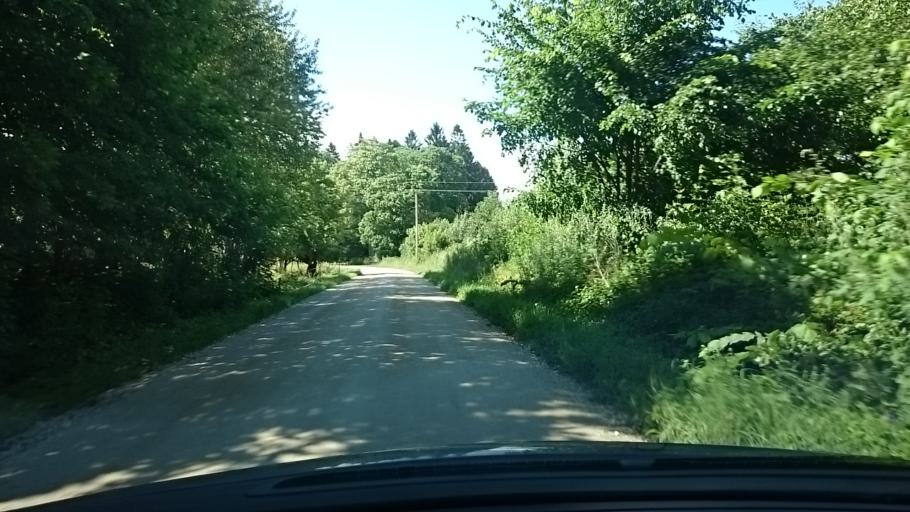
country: EE
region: Laeaene
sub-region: Haapsalu linn
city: Haapsalu
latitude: 59.0066
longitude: 23.5295
